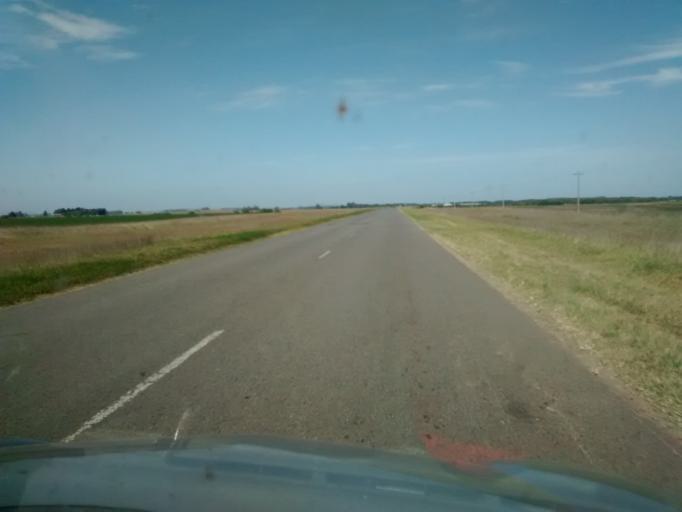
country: AR
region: Buenos Aires
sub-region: Partido de Balcarce
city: Balcarce
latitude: -37.6254
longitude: -58.4978
